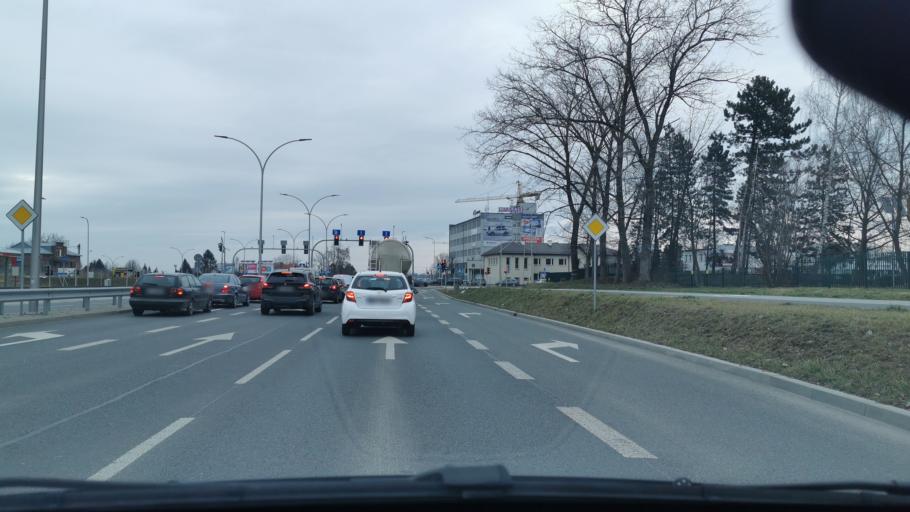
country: PL
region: Lublin Voivodeship
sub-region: Powiat lubelski
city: Lublin
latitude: 51.2462
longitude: 22.5069
